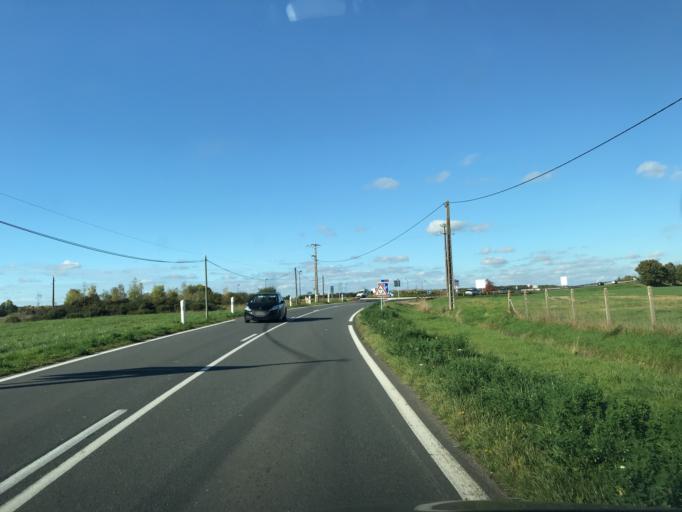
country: FR
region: Haute-Normandie
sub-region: Departement de l'Eure
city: Saint-Aubin-sur-Gaillon
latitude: 49.1296
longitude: 1.3108
